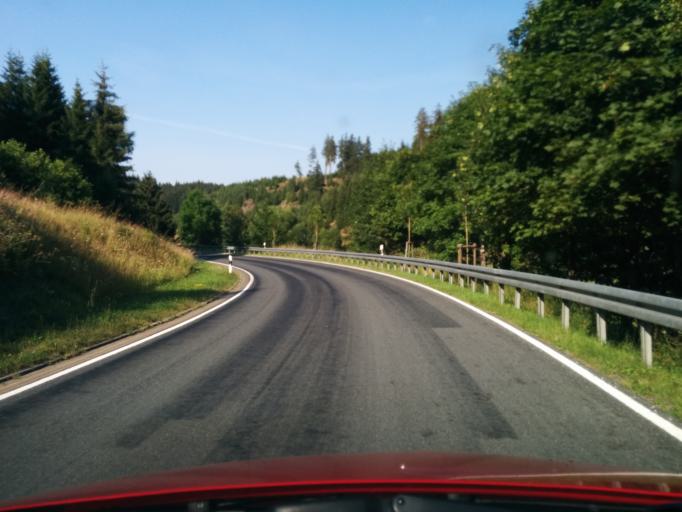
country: DE
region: Saxony-Anhalt
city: Elbingerode
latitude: 51.7213
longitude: 10.7648
